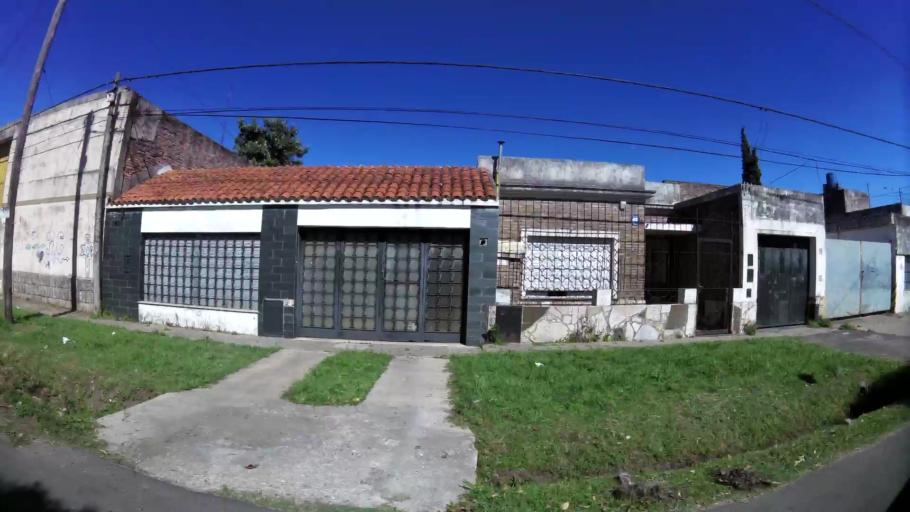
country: AR
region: Santa Fe
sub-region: Departamento de Rosario
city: Rosario
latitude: -32.9536
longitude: -60.6842
